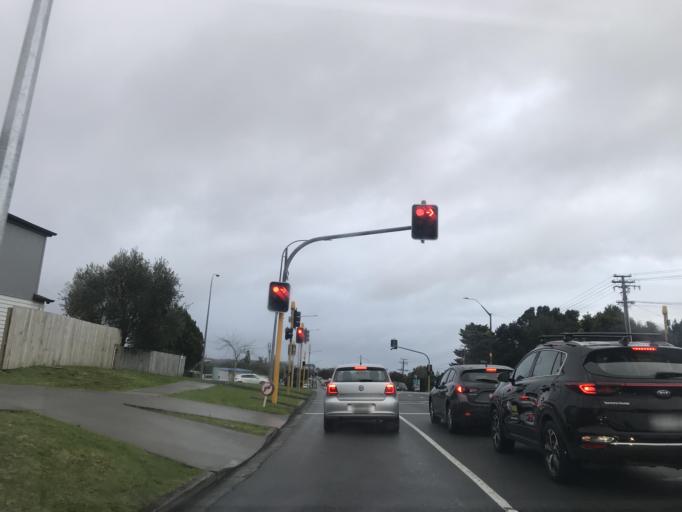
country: NZ
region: Auckland
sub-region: Auckland
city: Rothesay Bay
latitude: -36.7207
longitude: 174.7240
